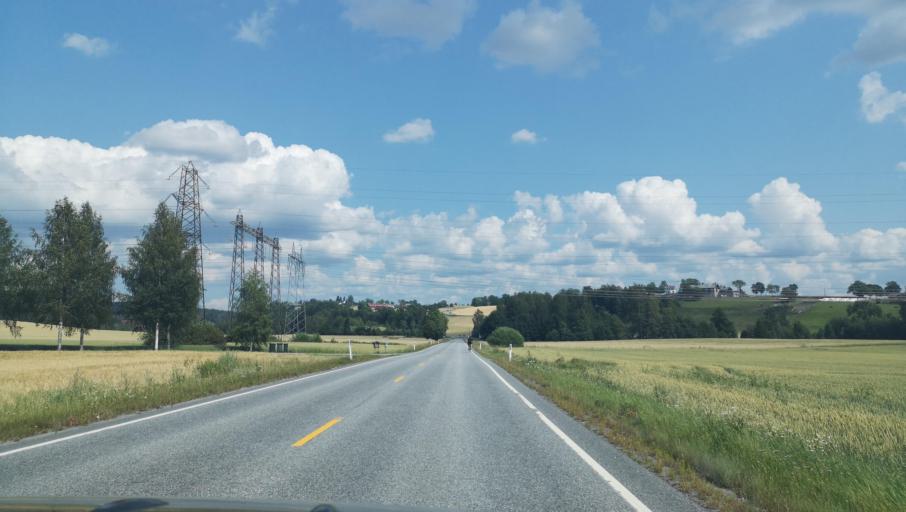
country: NO
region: Buskerud
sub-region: Ovre Eiker
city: Hokksund
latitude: 59.7225
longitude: 9.8298
